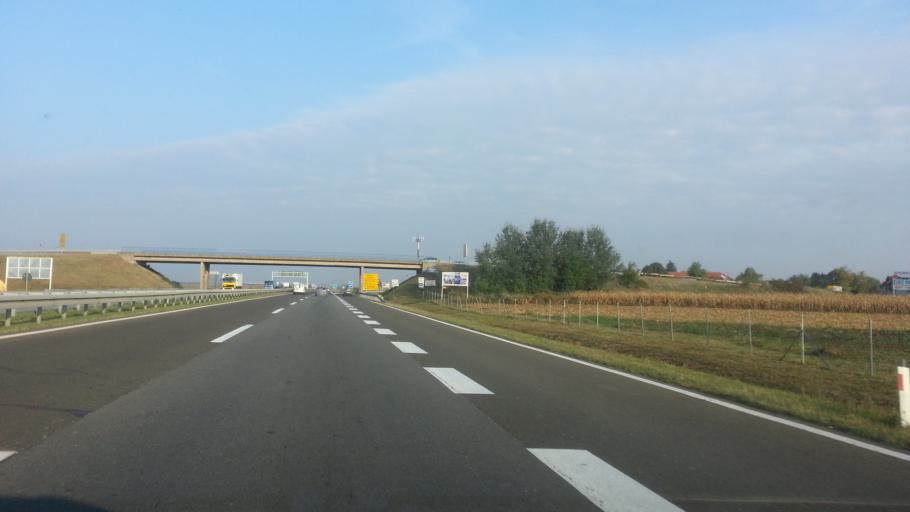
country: RS
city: Novi Banovci
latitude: 44.9427
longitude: 20.2832
